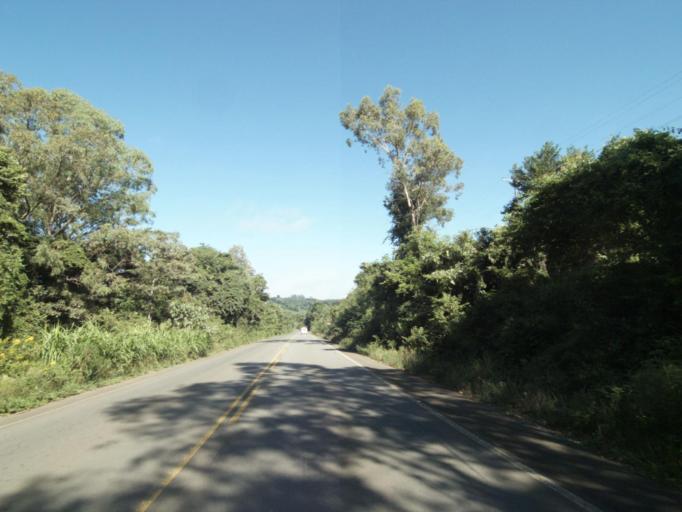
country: BR
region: Rio Grande do Sul
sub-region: Bento Goncalves
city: Bento Goncalves
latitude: -29.1211
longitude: -51.5489
